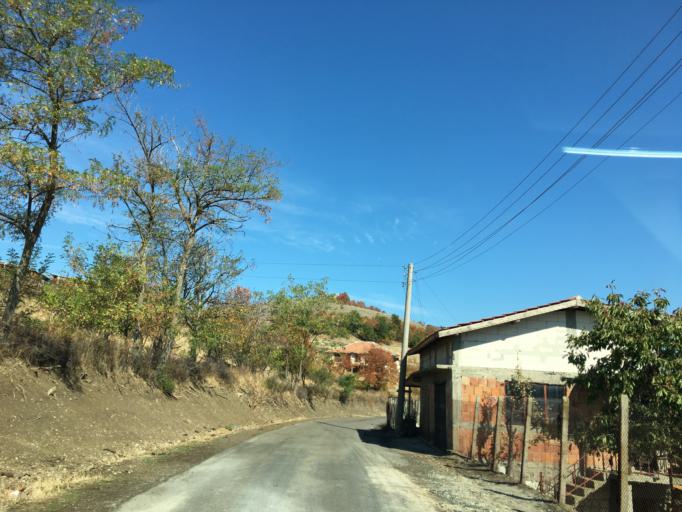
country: BG
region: Kurdzhali
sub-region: Obshtina Krumovgrad
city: Krumovgrad
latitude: 41.5059
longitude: 25.5235
